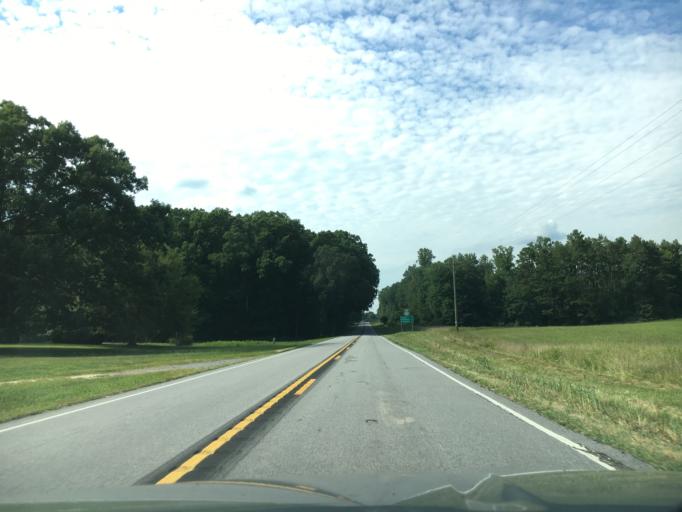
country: US
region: Virginia
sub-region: Halifax County
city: Mountain Road
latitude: 36.8940
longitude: -79.0169
